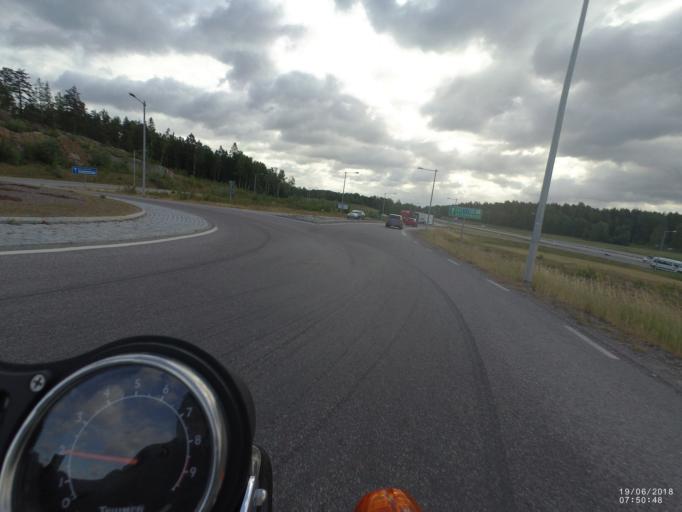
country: SE
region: Soedermanland
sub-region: Nykopings Kommun
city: Nykoping
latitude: 58.7733
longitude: 17.0281
